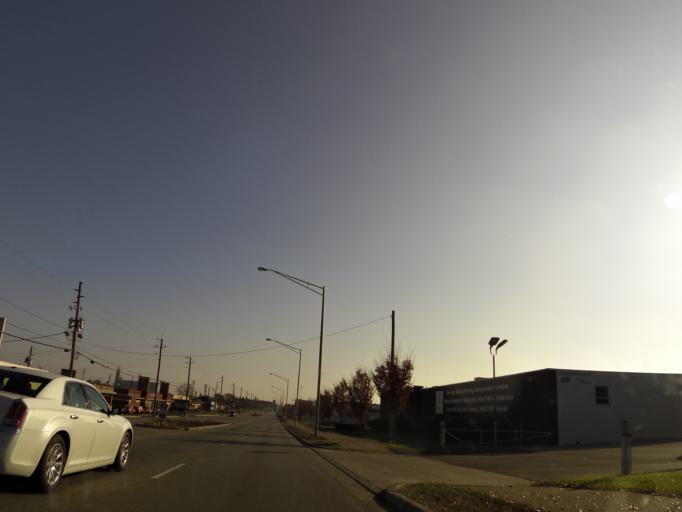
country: US
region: Indiana
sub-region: Marion County
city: Indianapolis
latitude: 39.7893
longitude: -86.1953
